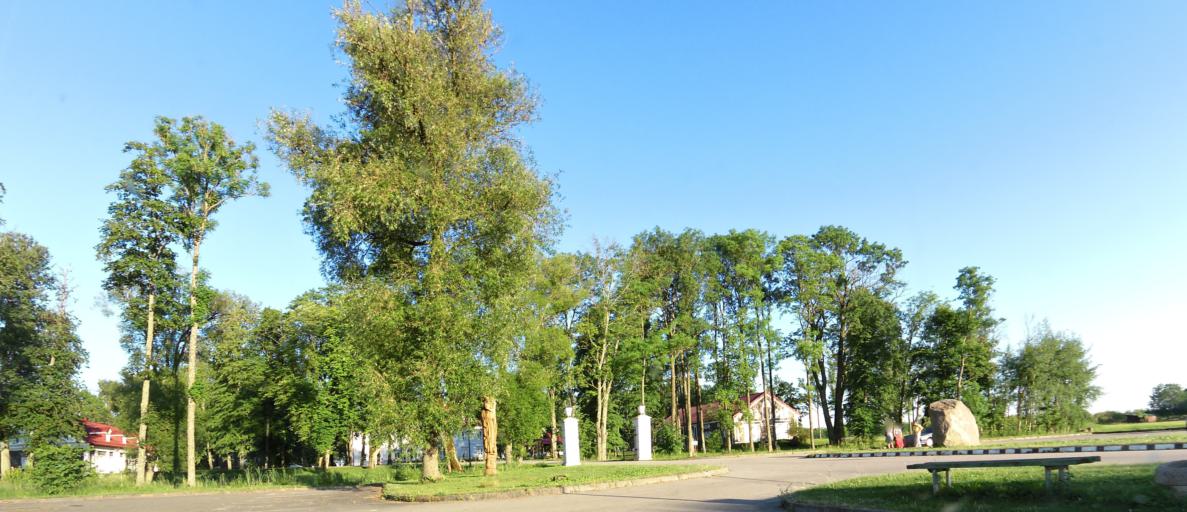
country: LT
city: Ramygala
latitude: 55.5979
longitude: 24.3549
